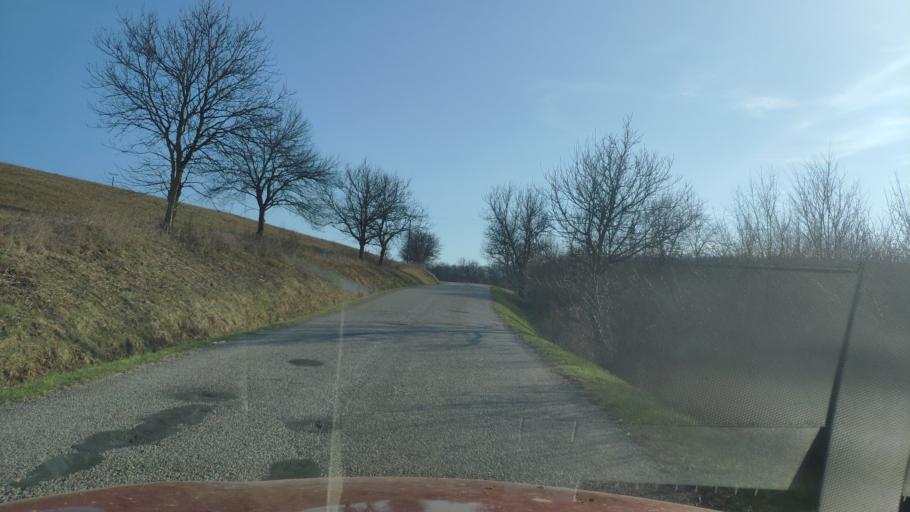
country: SK
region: Banskobystricky
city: Revuca
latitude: 48.5024
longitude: 20.2564
